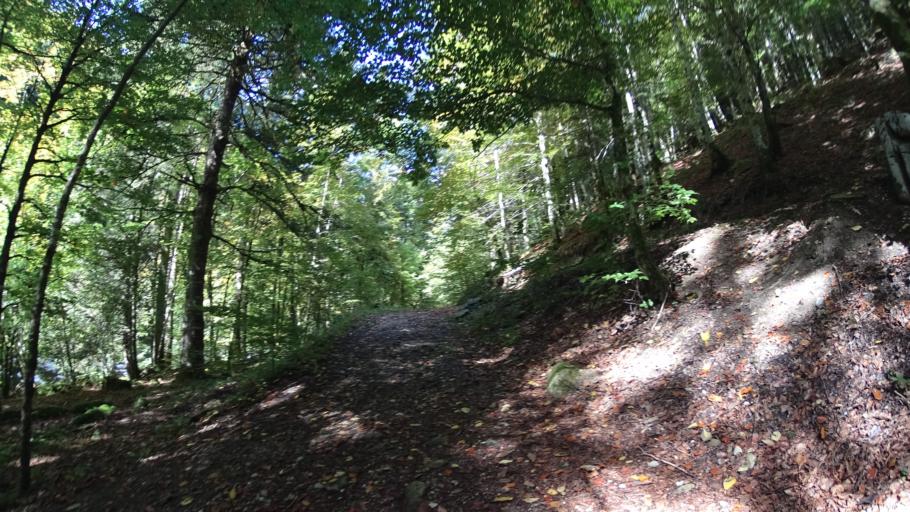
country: ES
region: Navarre
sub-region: Provincia de Navarra
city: Orbara
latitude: 42.9830
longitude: -1.1267
